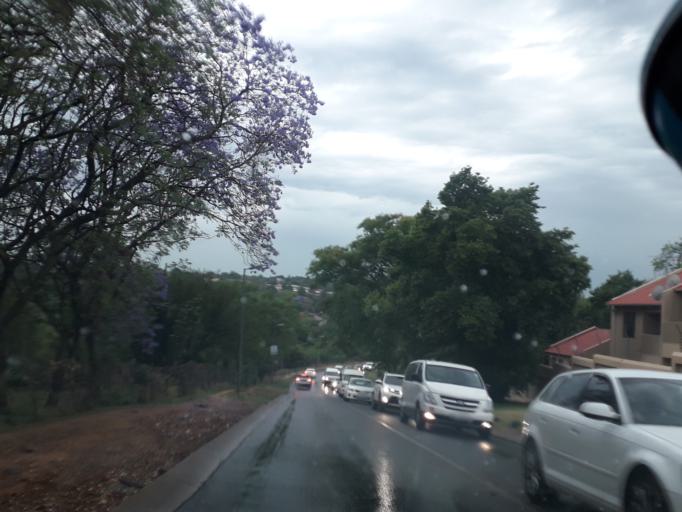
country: ZA
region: Gauteng
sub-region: City of Johannesburg Metropolitan Municipality
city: Johannesburg
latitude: -26.0784
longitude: 27.9831
